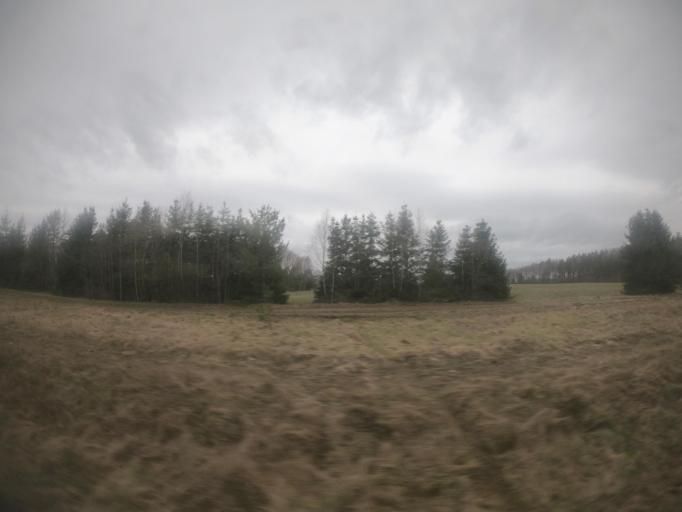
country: PL
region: West Pomeranian Voivodeship
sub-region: Powiat szczecinecki
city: Bialy Bor
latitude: 53.8133
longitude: 16.8678
